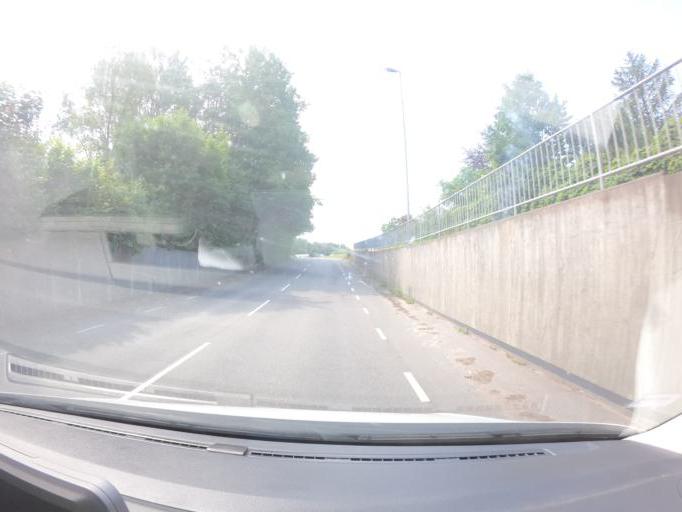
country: SE
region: Skane
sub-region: Hassleholms Kommun
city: Tormestorp
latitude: 56.1697
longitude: 13.6952
